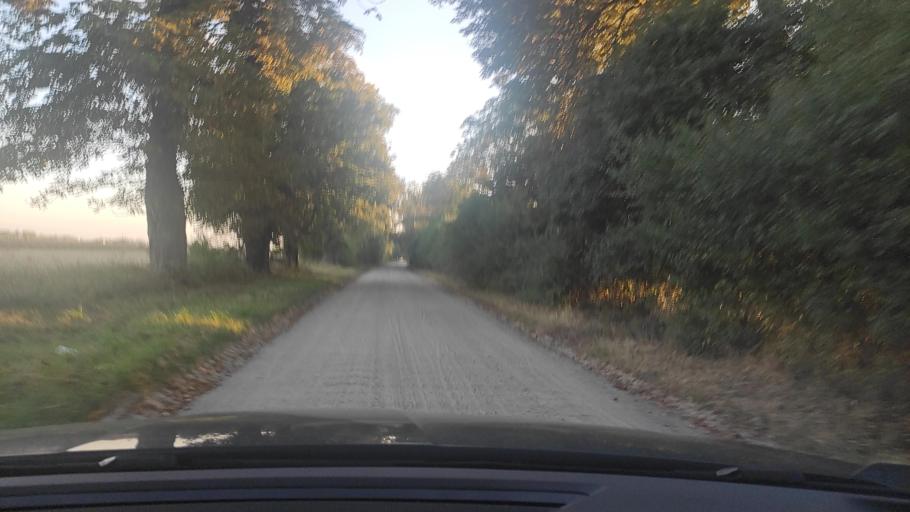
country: PL
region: Greater Poland Voivodeship
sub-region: Powiat poznanski
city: Swarzedz
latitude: 52.4380
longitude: 17.1215
